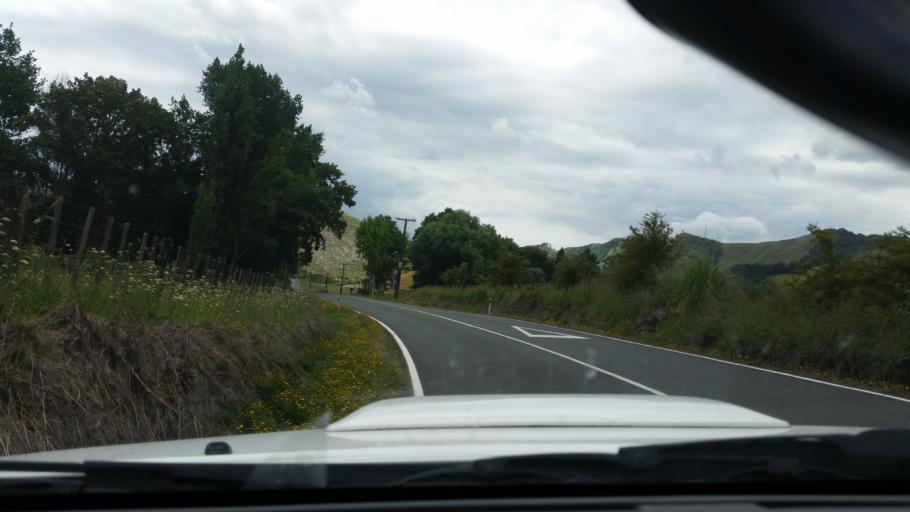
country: NZ
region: Northland
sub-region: Kaipara District
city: Dargaville
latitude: -35.7462
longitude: 173.8774
